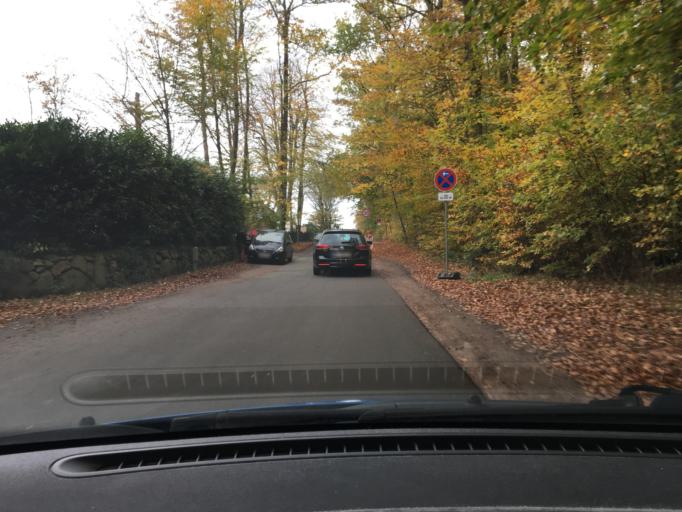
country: DE
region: Lower Saxony
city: Seevetal
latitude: 53.4140
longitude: 9.9898
